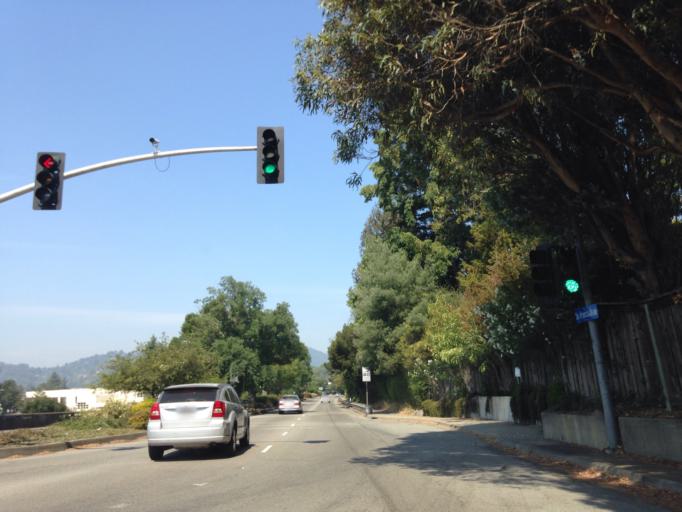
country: US
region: California
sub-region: Marin County
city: Larkspur
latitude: 37.9506
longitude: -122.5336
